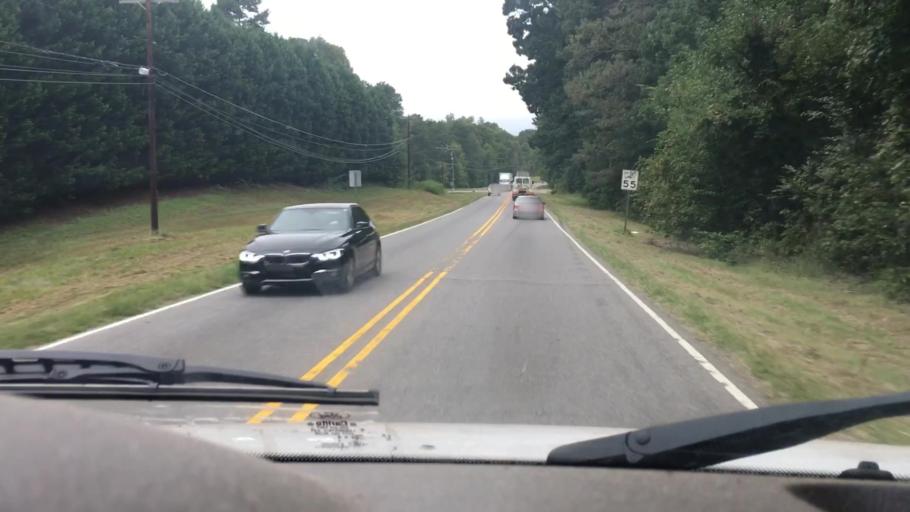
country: US
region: North Carolina
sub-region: Catawba County
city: Lake Norman of Catawba
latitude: 35.6022
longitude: -80.9214
